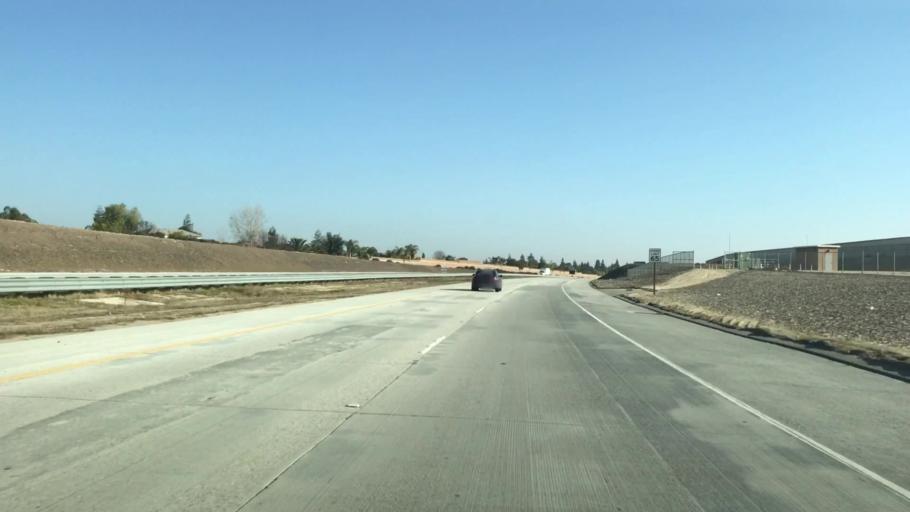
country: US
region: California
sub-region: Kern County
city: Rosedale
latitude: 35.3573
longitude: -119.1718
